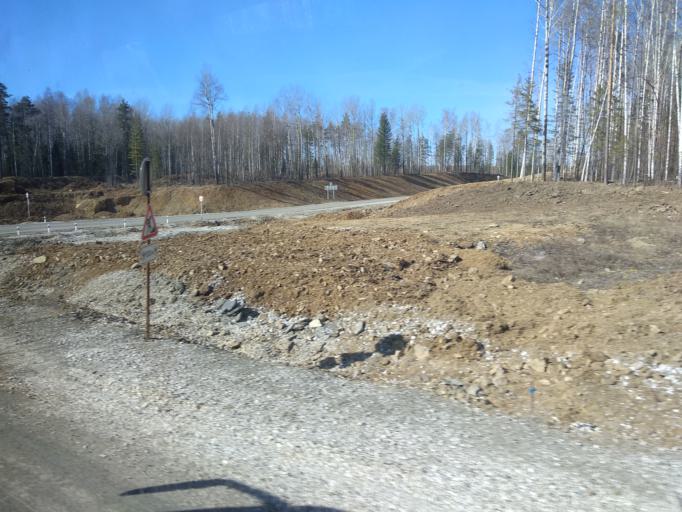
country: RU
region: Sverdlovsk
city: Krasnotur'insk
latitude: 59.6688
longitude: 60.1825
